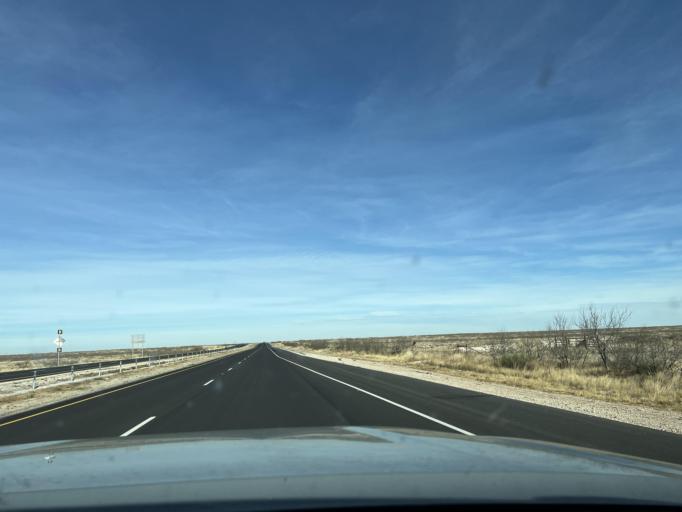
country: US
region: Texas
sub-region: Ector County
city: Gardendale
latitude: 32.0295
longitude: -102.4322
